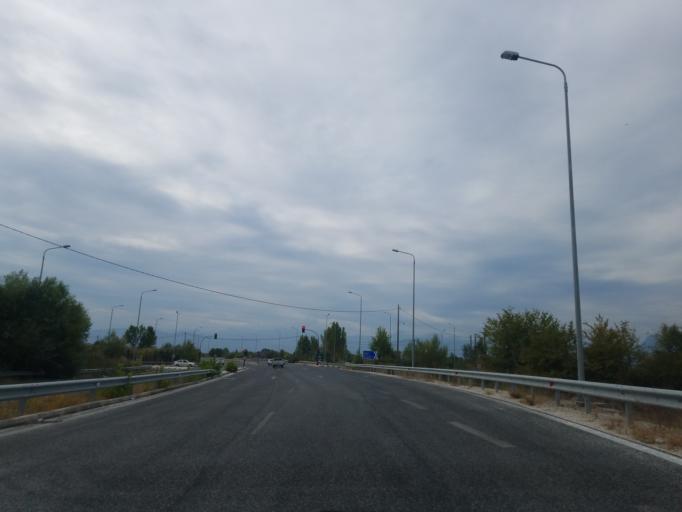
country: GR
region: Thessaly
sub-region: Trikala
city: Pyrgetos
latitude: 39.5590
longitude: 21.7343
